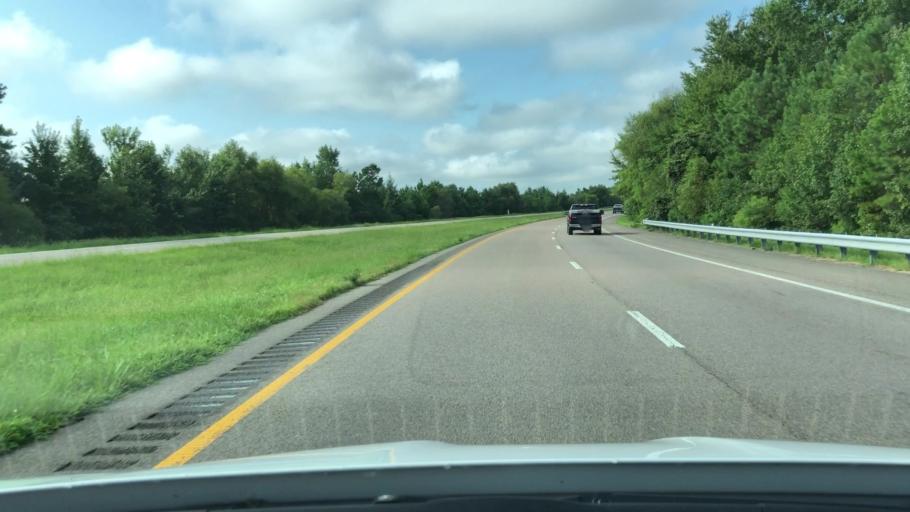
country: US
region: Virginia
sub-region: City of Portsmouth
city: Portsmouth Heights
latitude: 36.6783
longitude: -76.3473
